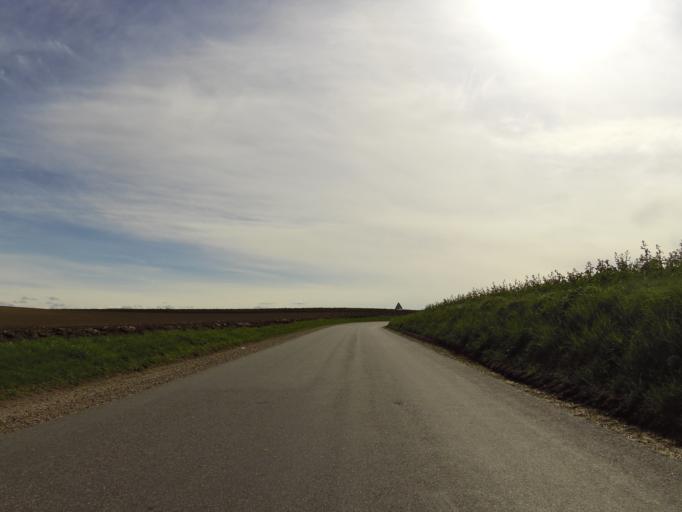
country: DK
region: Central Jutland
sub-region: Skive Kommune
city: Skive
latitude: 56.5460
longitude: 8.9633
